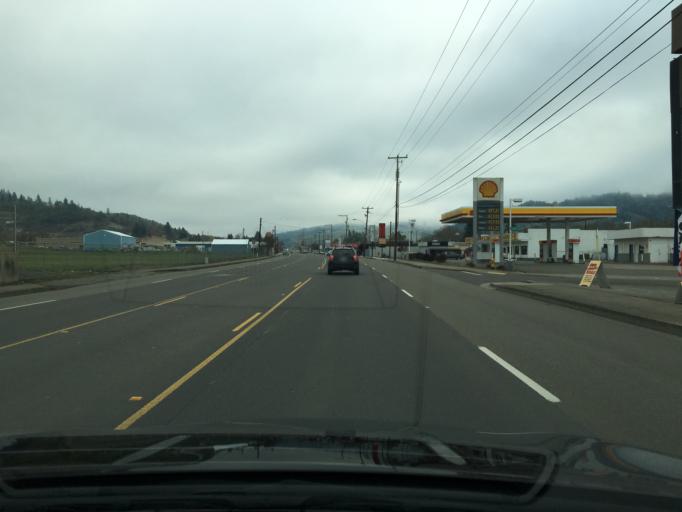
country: US
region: Oregon
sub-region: Douglas County
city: Roseburg
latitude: 43.2131
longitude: -123.3305
